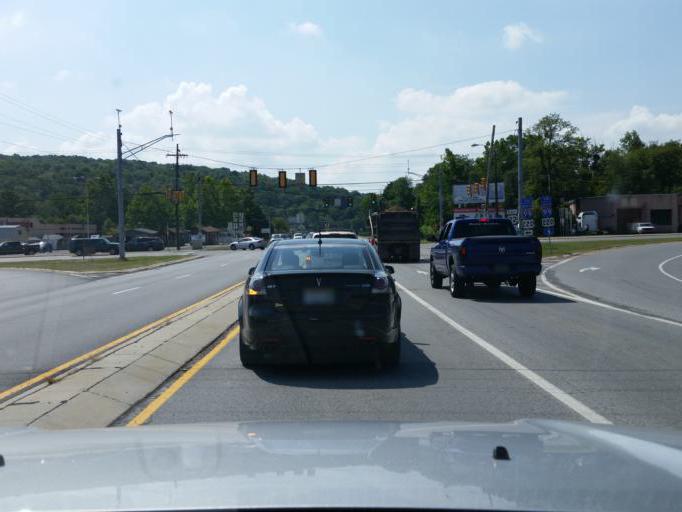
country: US
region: Pennsylvania
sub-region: Blair County
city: Duncansville
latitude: 40.4222
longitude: -78.4403
